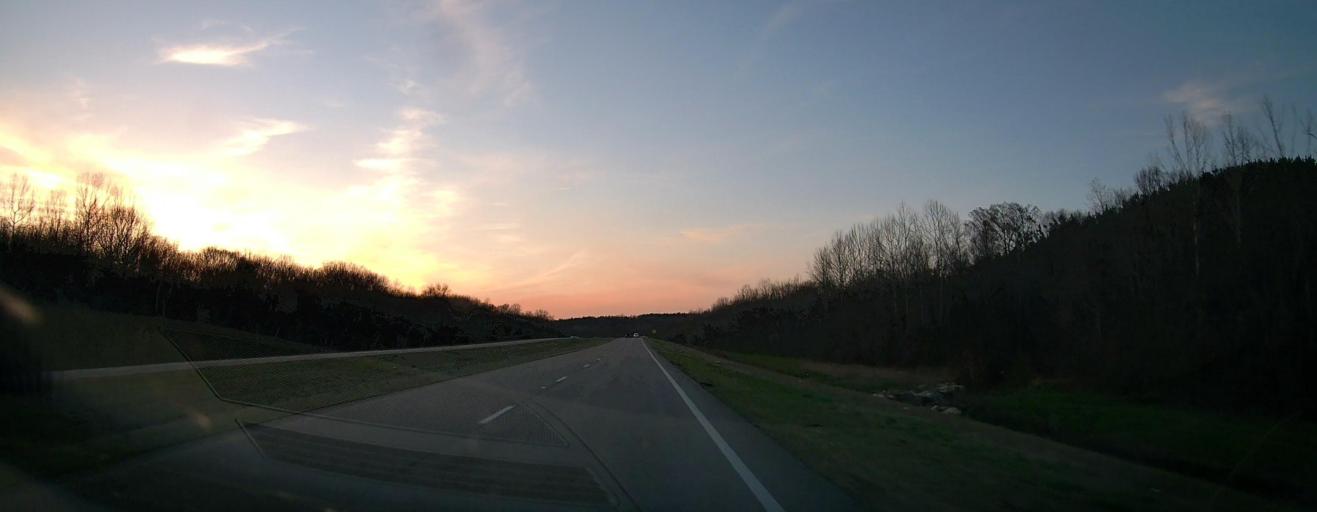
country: US
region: Mississippi
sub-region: Alcorn County
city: Corinth
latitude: 34.9411
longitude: -88.7802
